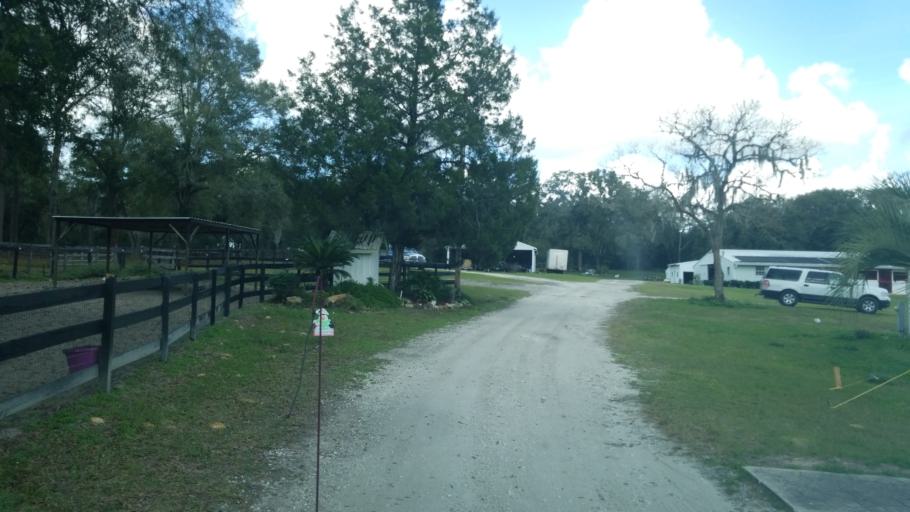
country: US
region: Florida
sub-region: Marion County
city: Ocala
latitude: 29.1551
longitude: -82.2583
